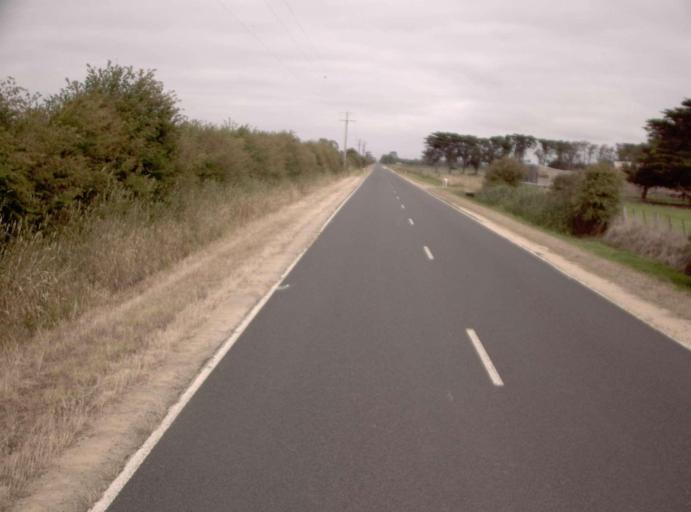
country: AU
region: Victoria
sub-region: Wellington
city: Sale
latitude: -38.0527
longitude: 146.9582
